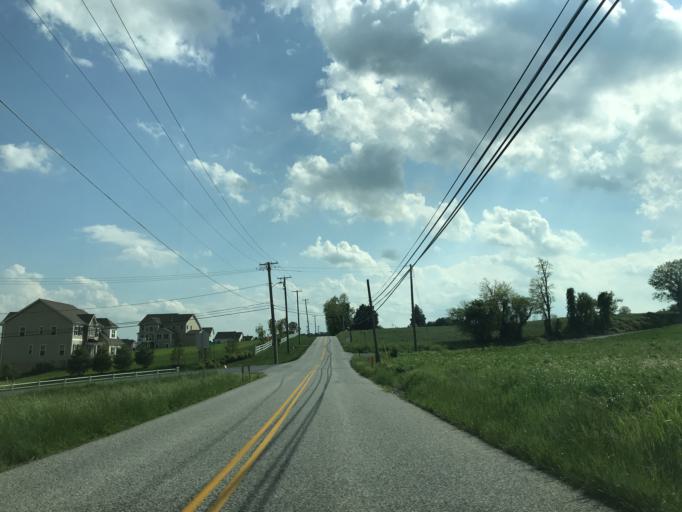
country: US
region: Maryland
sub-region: Harford County
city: Bel Air North
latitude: 39.5998
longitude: -76.3767
